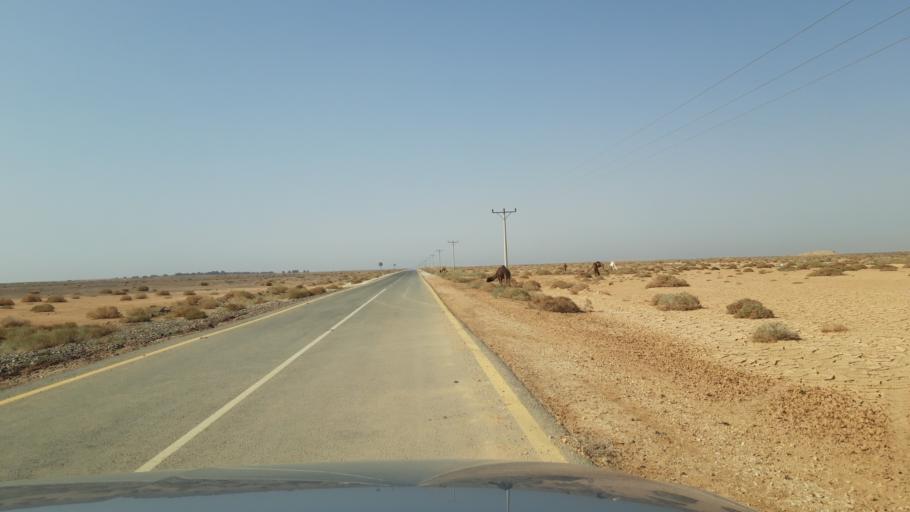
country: JO
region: Amman
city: Al Azraq ash Shamali
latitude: 31.7766
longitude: 36.7716
